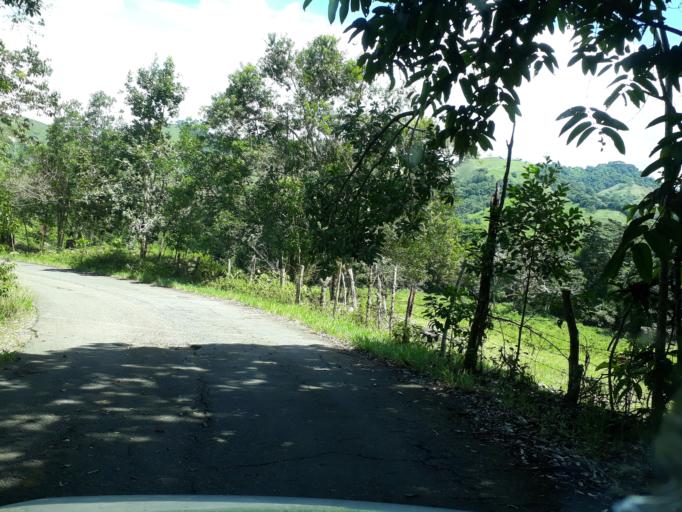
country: CO
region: Cundinamarca
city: Medina
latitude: 4.5778
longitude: -73.3250
